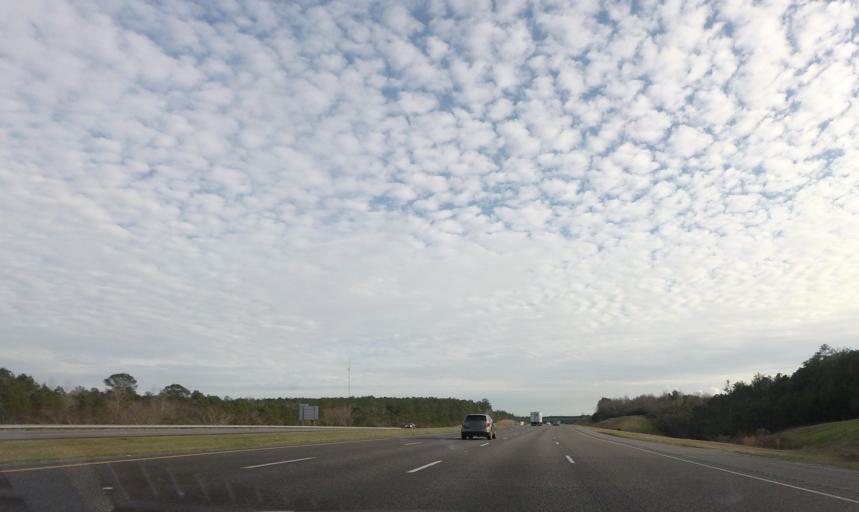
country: US
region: Alabama
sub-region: Walker County
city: Dora
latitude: 33.6761
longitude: -87.0796
